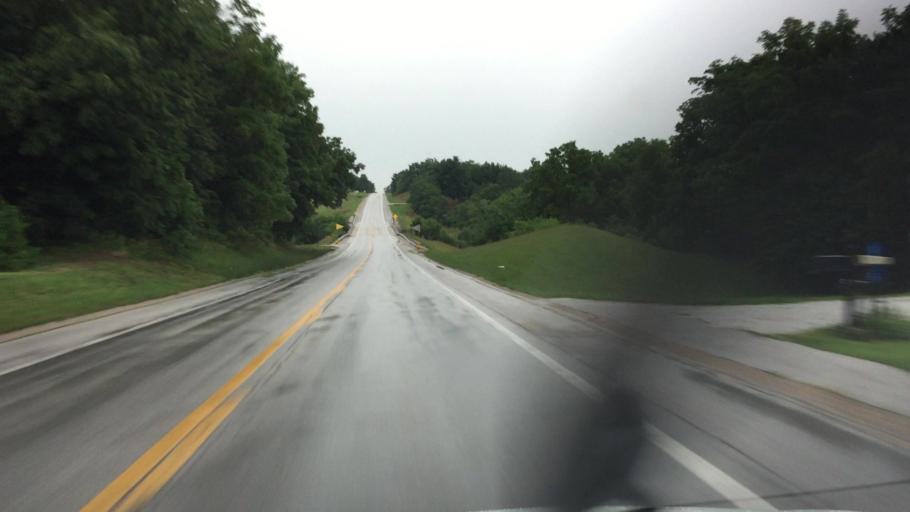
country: US
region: Illinois
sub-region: Hancock County
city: Carthage
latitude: 40.4287
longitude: -91.1401
